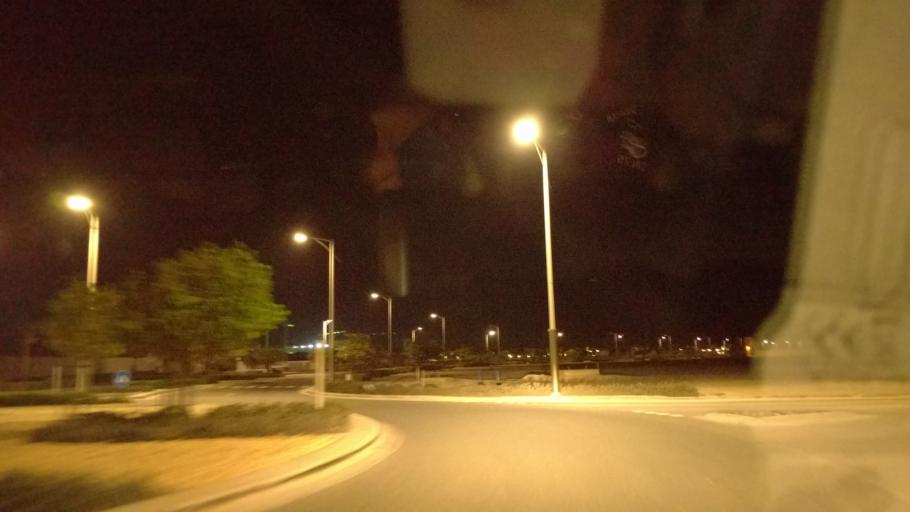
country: AE
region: Abu Dhabi
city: Abu Dhabi
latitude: 24.5531
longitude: 54.4526
